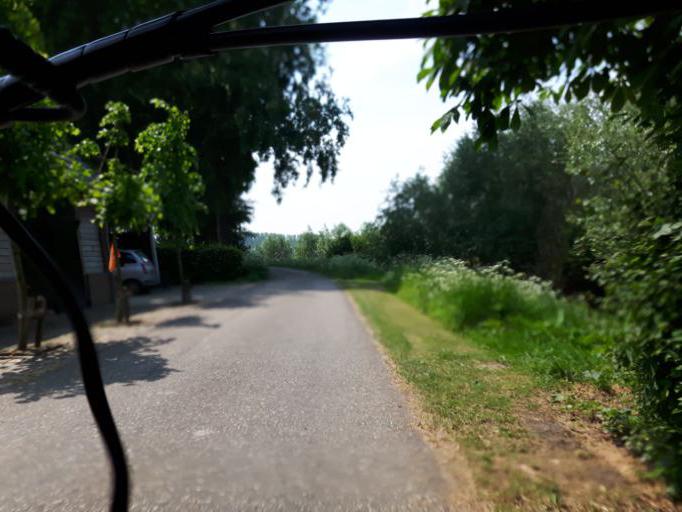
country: NL
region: North Brabant
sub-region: Gemeente Steenbergen
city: Welberg
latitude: 51.5728
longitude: 4.3466
